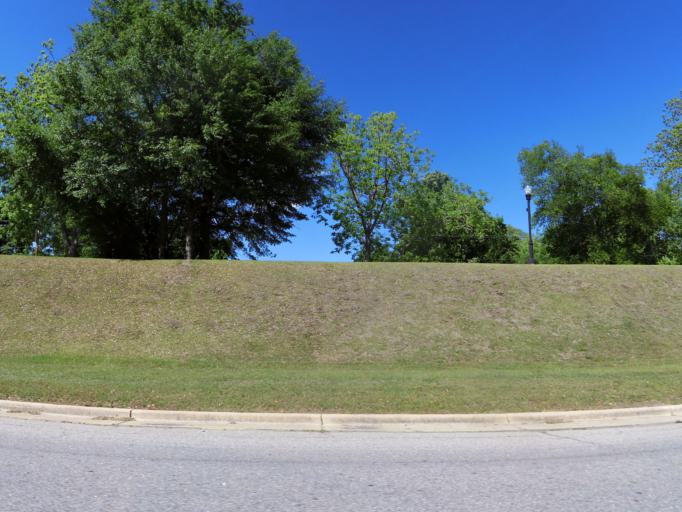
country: US
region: South Carolina
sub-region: Barnwell County
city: Williston
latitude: 33.3977
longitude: -81.4144
